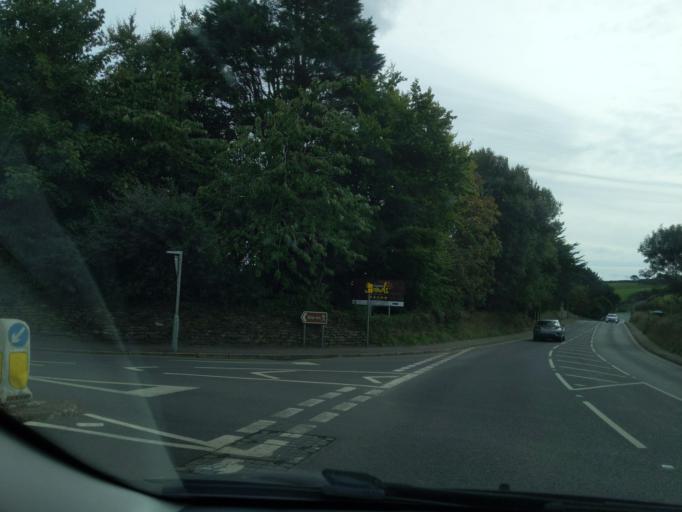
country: GB
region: England
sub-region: Cornwall
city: Mevagissey
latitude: 50.2918
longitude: -4.7861
